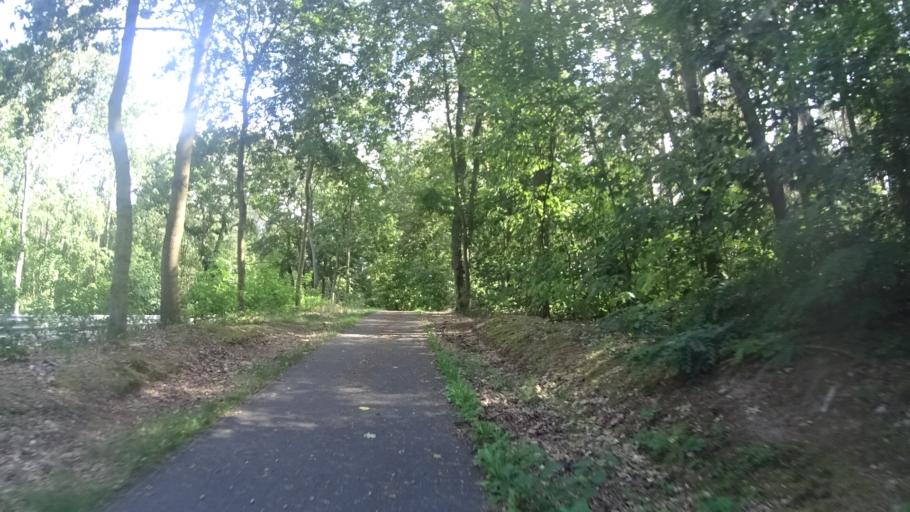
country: DE
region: Brandenburg
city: Rhinow
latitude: 52.7261
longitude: 12.3570
